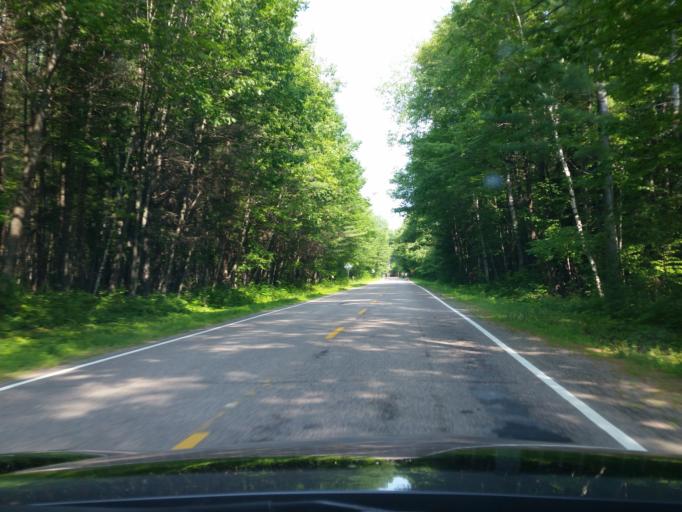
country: CA
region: Quebec
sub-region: Outaouais
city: Shawville
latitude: 45.5217
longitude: -76.4323
